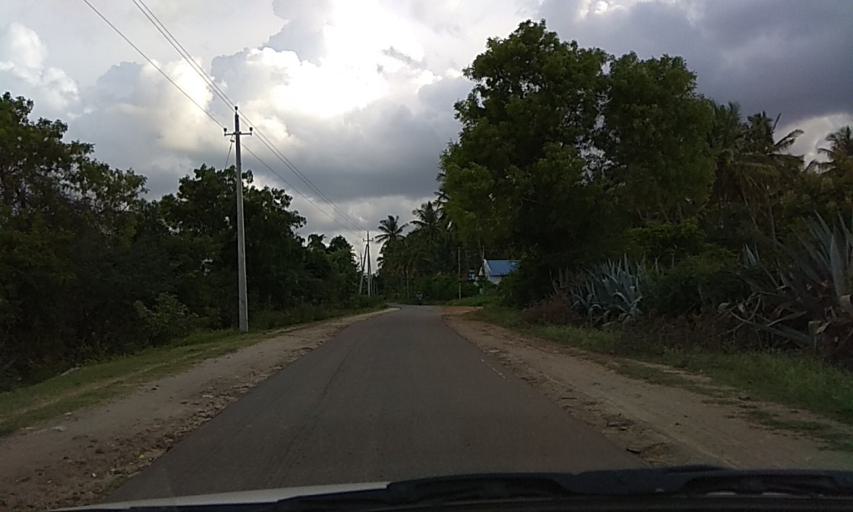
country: IN
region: Karnataka
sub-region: Chamrajnagar
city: Gundlupet
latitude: 11.8793
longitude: 76.7473
